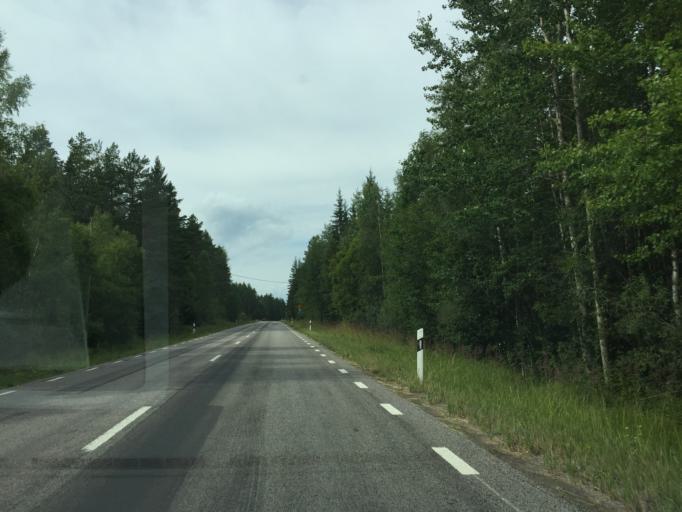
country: SE
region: Uppsala
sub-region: Tierps Kommun
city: Tierp
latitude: 60.3626
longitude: 17.3087
